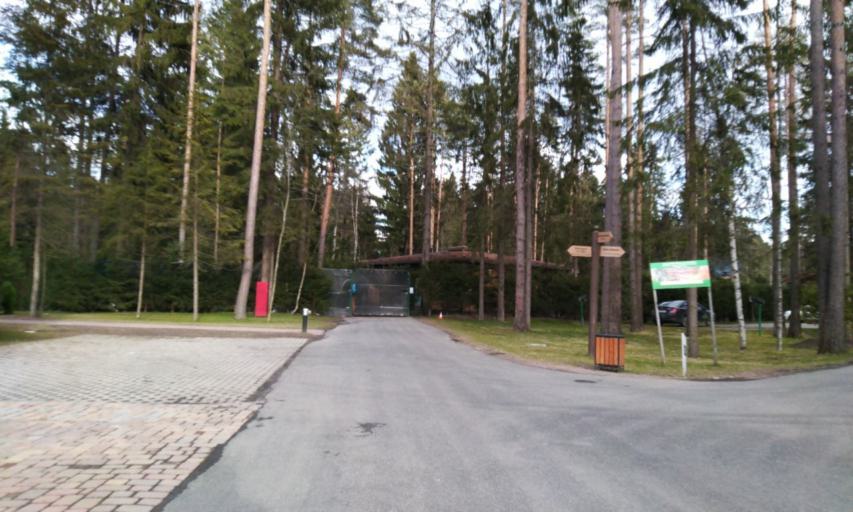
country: RU
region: Leningrad
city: Toksovo
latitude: 60.1301
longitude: 30.4485
